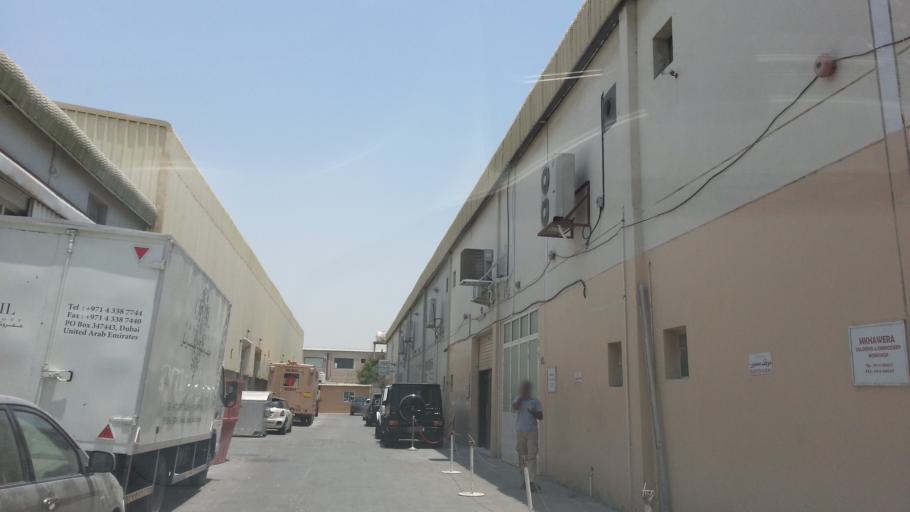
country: AE
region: Dubai
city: Dubai
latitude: 25.1509
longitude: 55.2281
